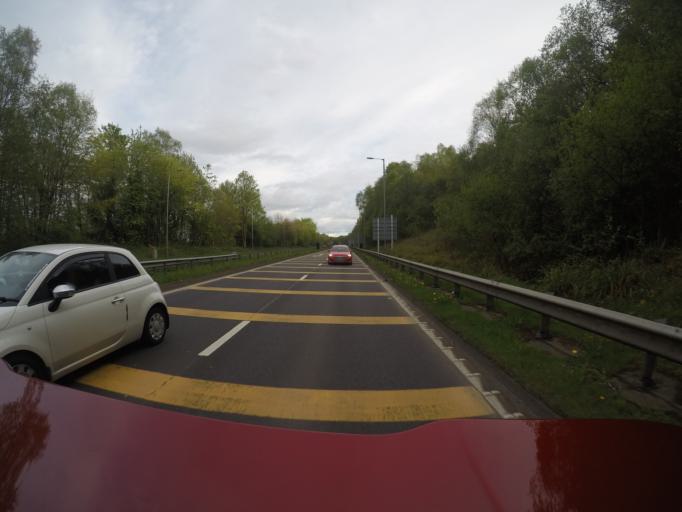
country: GB
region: Scotland
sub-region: West Dunbartonshire
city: Alexandria
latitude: 55.9972
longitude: -4.5966
